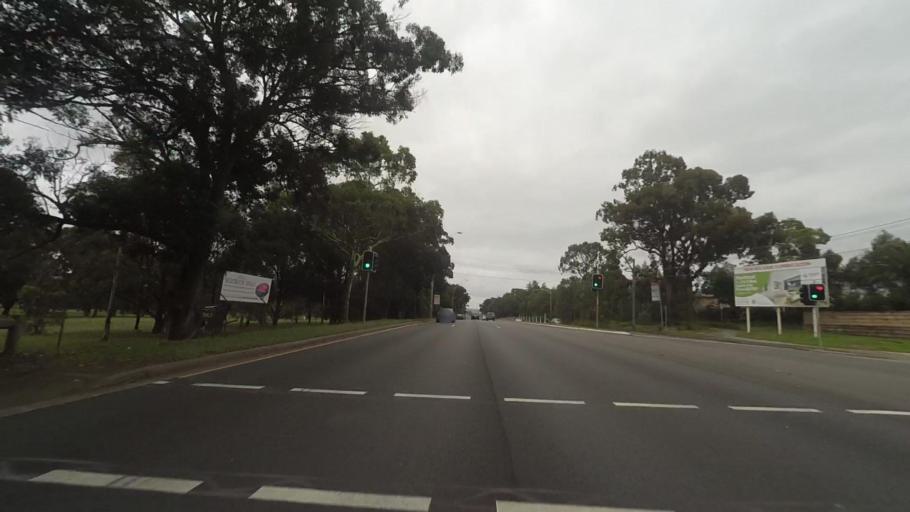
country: AU
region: New South Wales
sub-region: Auburn
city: Berala
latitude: -33.8781
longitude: 151.0411
